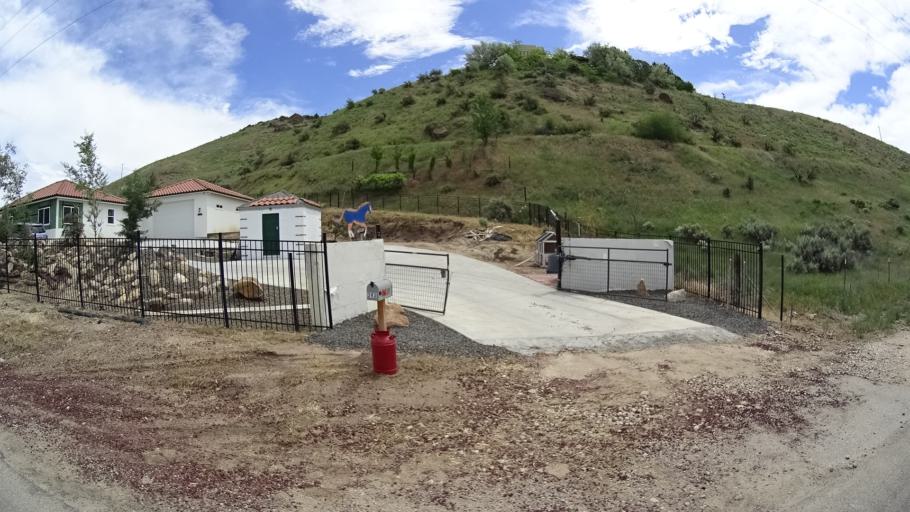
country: US
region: Idaho
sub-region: Ada County
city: Boise
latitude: 43.5951
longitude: -116.1632
